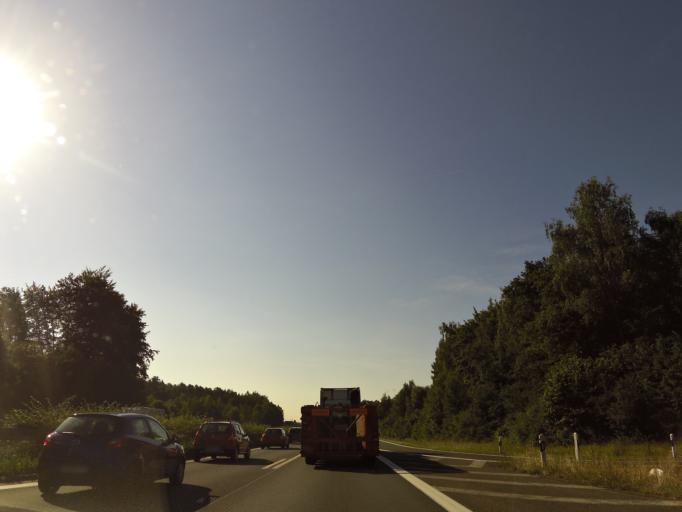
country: DE
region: Bavaria
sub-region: Regierungsbezirk Mittelfranken
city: Obermichelbach
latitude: 49.5681
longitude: 10.9408
